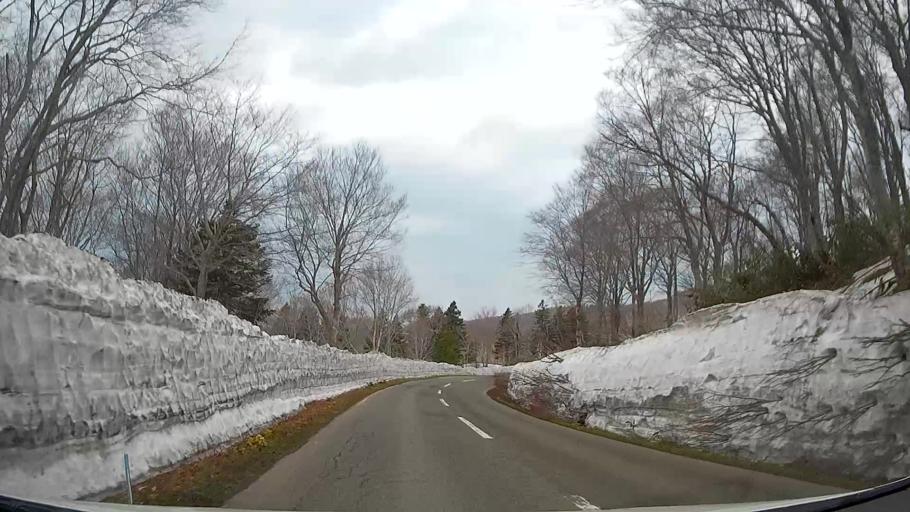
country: JP
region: Aomori
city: Aomori Shi
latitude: 40.6456
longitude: 140.8583
